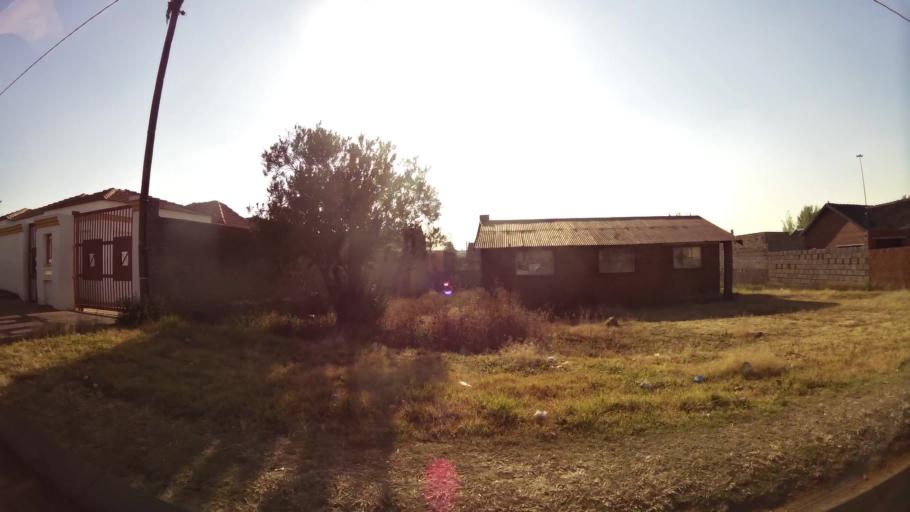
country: ZA
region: Gauteng
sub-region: City of Johannesburg Metropolitan Municipality
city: Soweto
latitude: -26.2652
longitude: 27.8701
